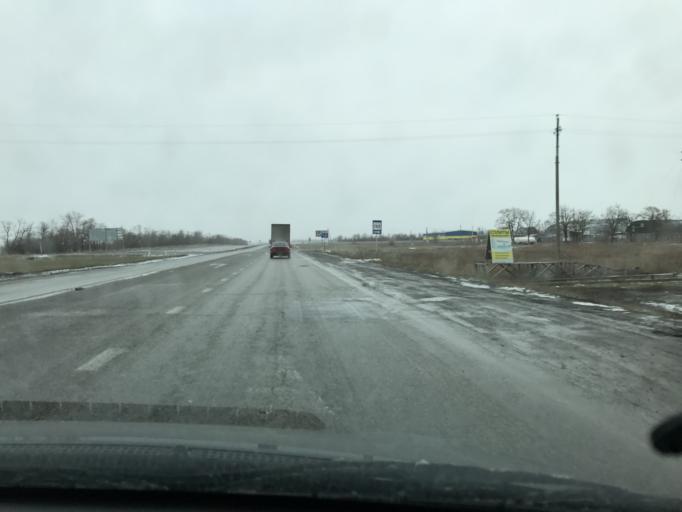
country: RU
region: Rostov
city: Kagal'nitskaya
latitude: 46.8753
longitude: 40.1601
